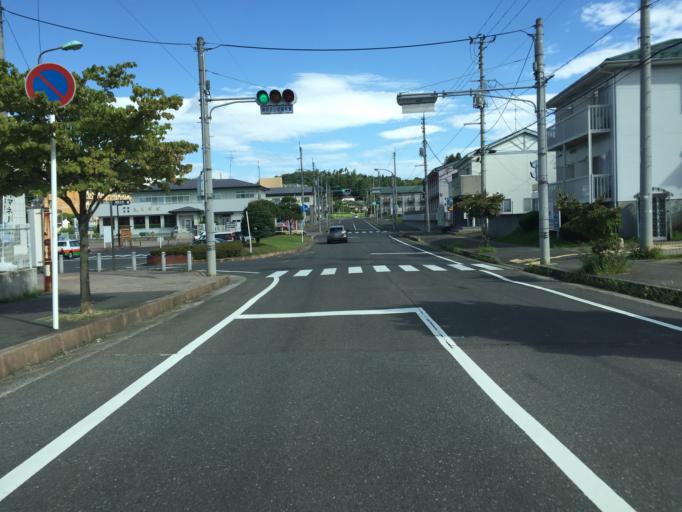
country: JP
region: Fukushima
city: Fukushima-shi
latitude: 37.6803
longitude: 140.4531
